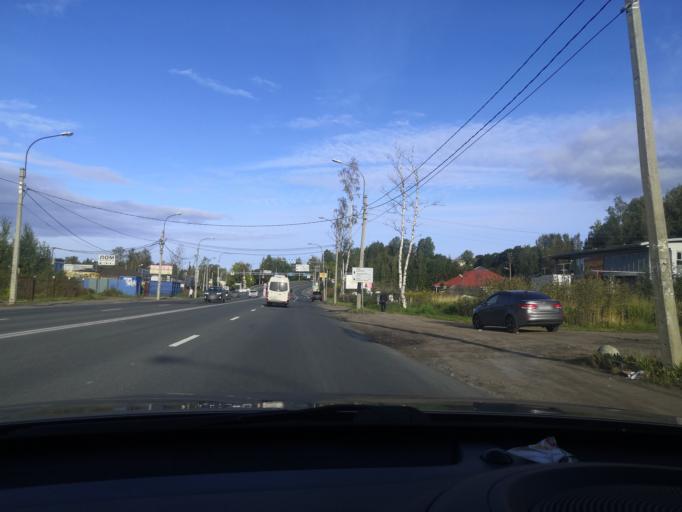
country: RU
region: St.-Petersburg
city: Pargolovo
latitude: 60.0780
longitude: 30.2693
